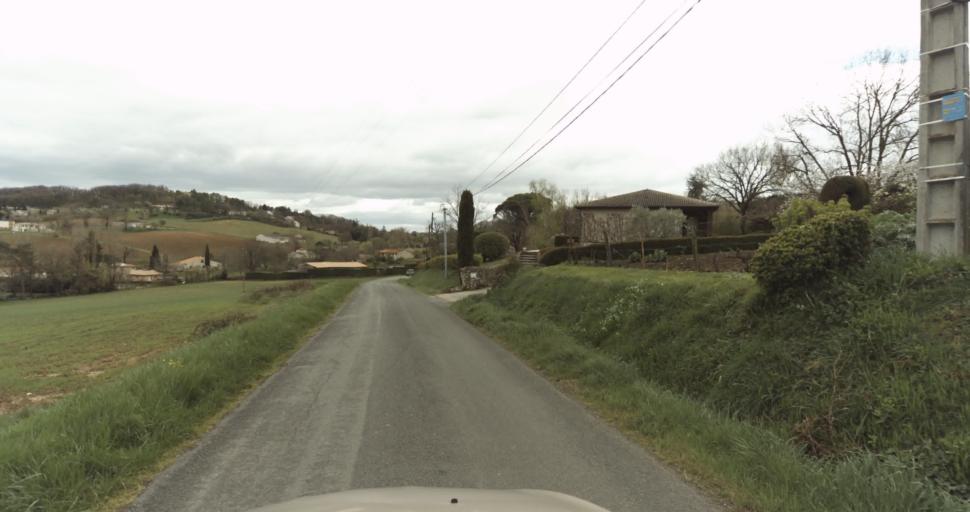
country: FR
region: Midi-Pyrenees
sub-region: Departement du Tarn
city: Puygouzon
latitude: 43.9070
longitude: 2.1668
